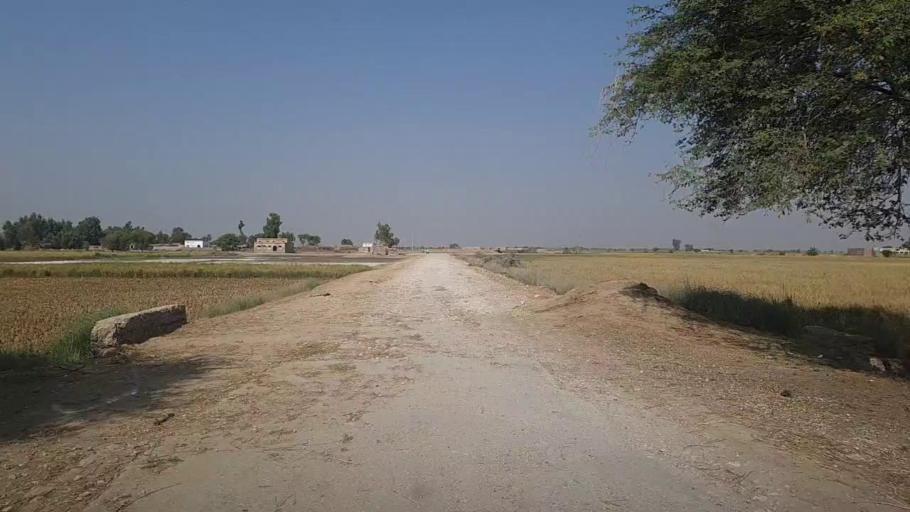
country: PK
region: Sindh
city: Kandhkot
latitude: 28.3932
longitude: 69.3263
